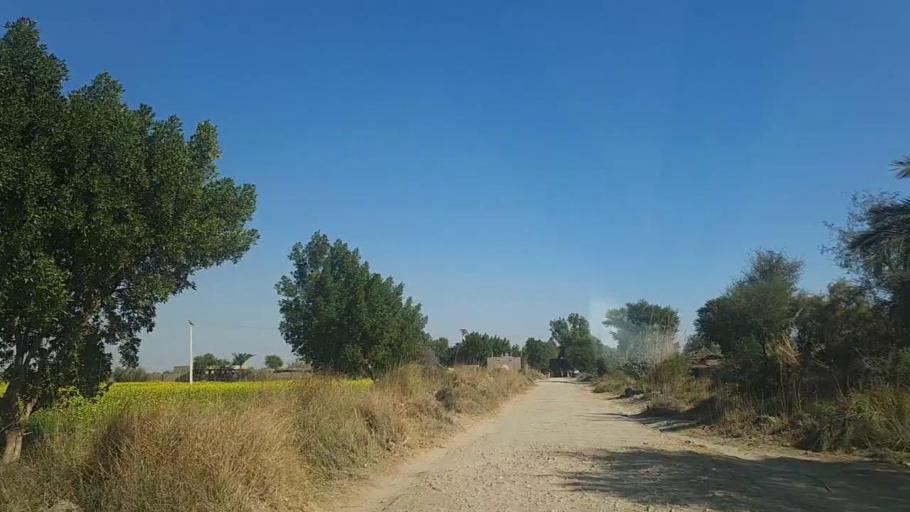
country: PK
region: Sindh
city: Sanghar
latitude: 26.2092
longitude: 68.9110
